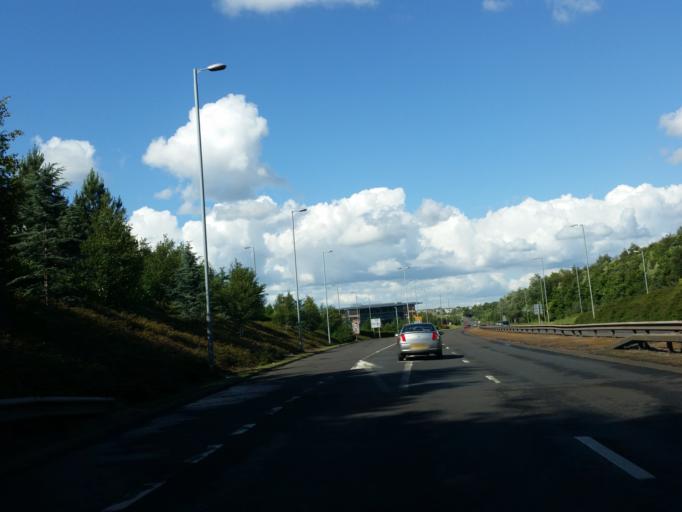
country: GB
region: Scotland
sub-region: North Lanarkshire
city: Bellshill
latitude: 55.8282
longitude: -4.0352
